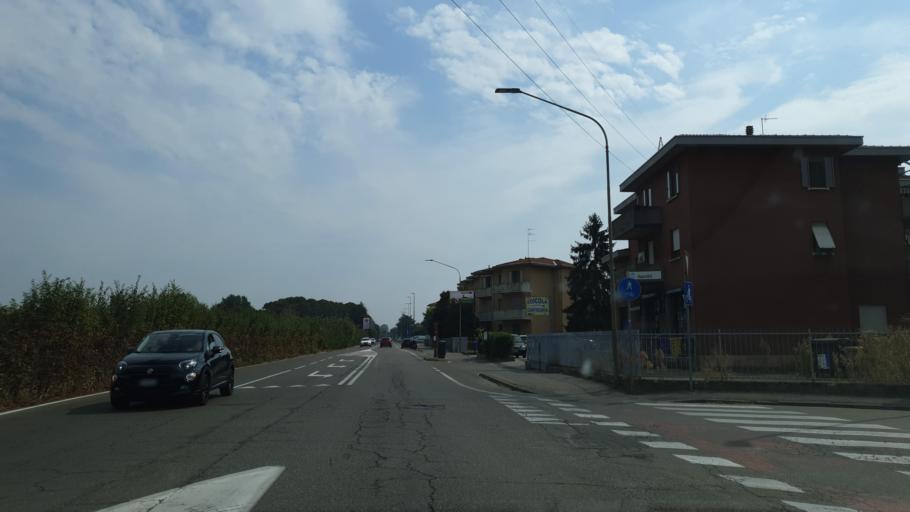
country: IT
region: Emilia-Romagna
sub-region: Provincia di Parma
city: Vicofertile
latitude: 44.8202
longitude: 10.2846
